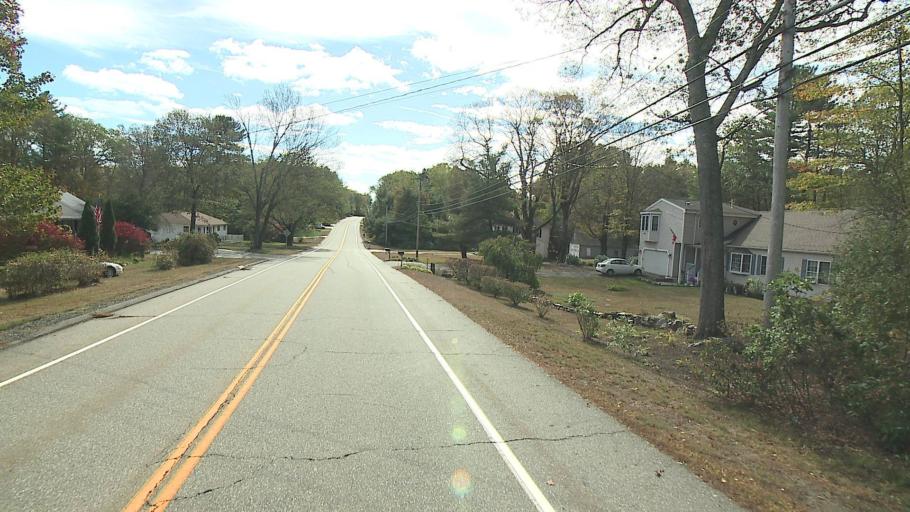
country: US
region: Connecticut
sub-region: Windham County
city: North Grosvenor Dale
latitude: 42.0002
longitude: -71.9001
